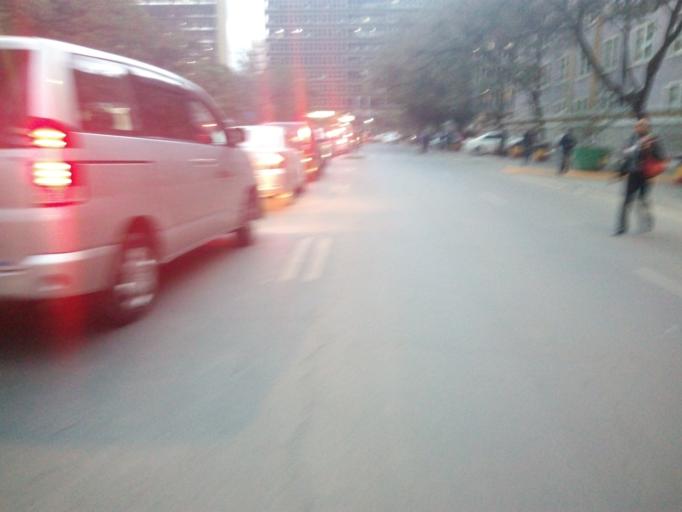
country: KE
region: Nairobi Area
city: Nairobi
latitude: -1.2877
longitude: 36.8244
